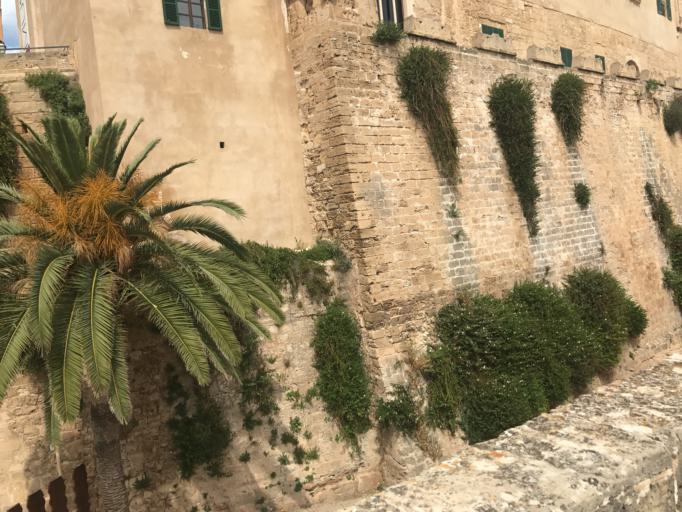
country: ES
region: Balearic Islands
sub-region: Illes Balears
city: Palma
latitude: 39.5667
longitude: 2.6488
